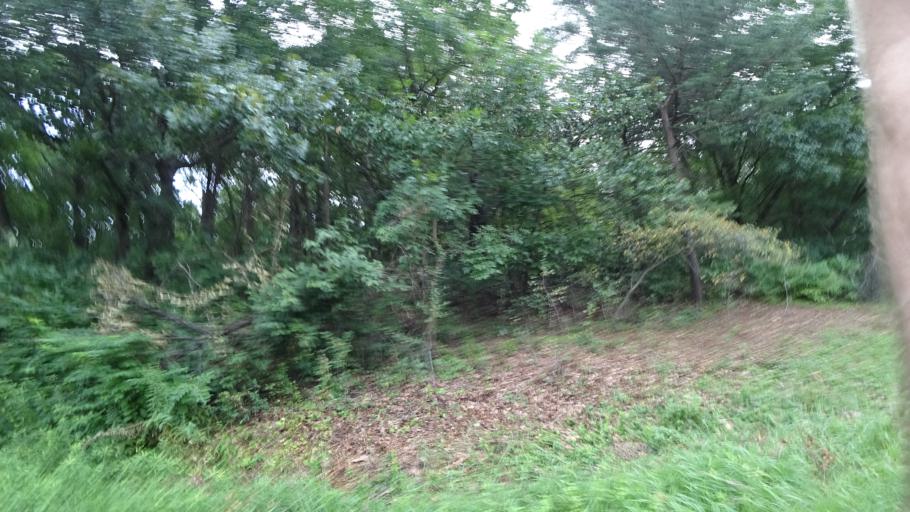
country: US
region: Maryland
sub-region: Prince George's County
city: Mount Rainier
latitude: 38.9088
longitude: -76.9767
